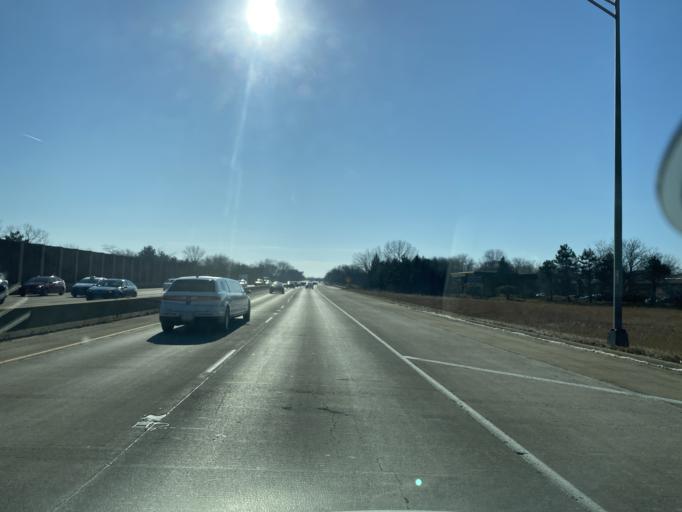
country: US
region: Illinois
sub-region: DuPage County
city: Clarendon Hills
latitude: 41.7872
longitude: -87.9470
